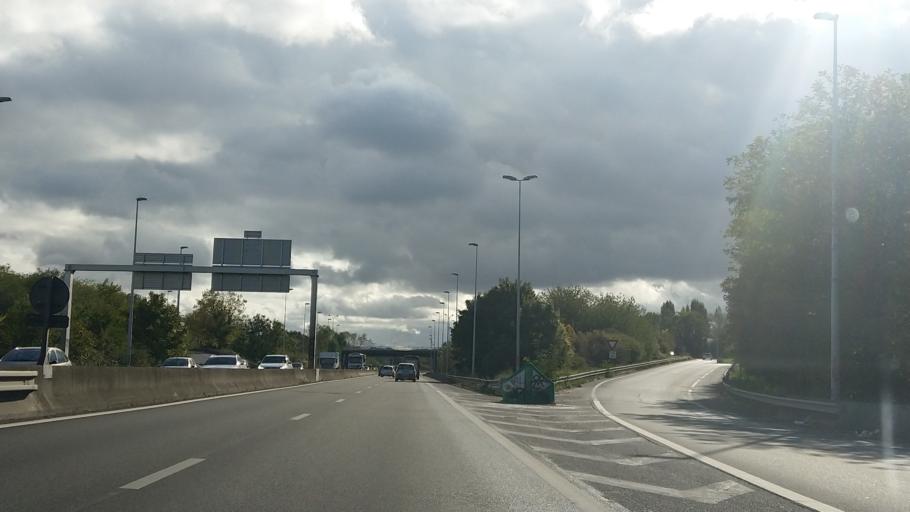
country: FR
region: Ile-de-France
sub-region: Departement du Val-d'Oise
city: Le Plessis-Bouchard
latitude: 49.0012
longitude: 2.2463
